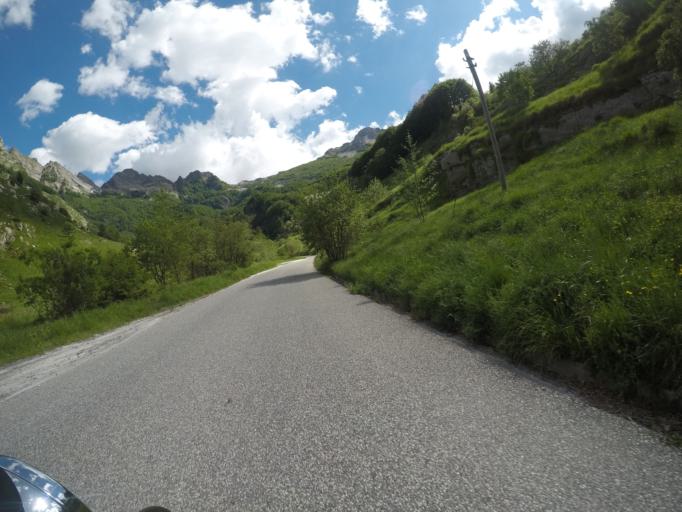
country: IT
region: Tuscany
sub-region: Provincia di Lucca
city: Minucciano
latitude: 44.1376
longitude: 10.1965
